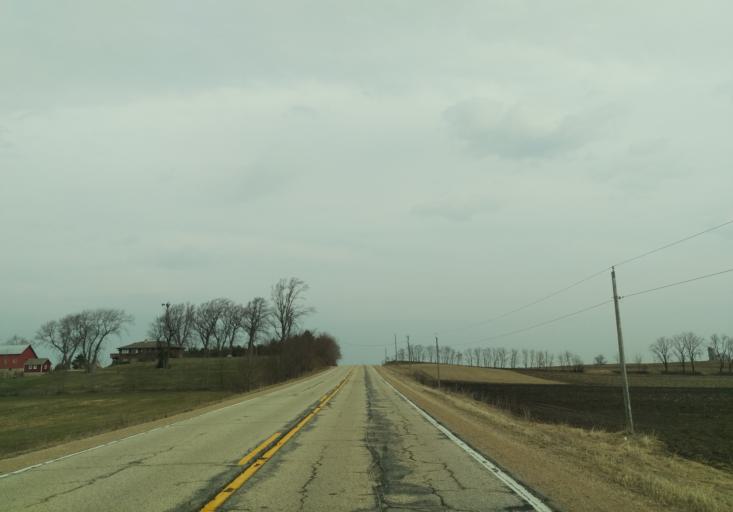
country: US
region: Wisconsin
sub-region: Dane County
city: Waunakee
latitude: 43.2442
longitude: -89.4616
